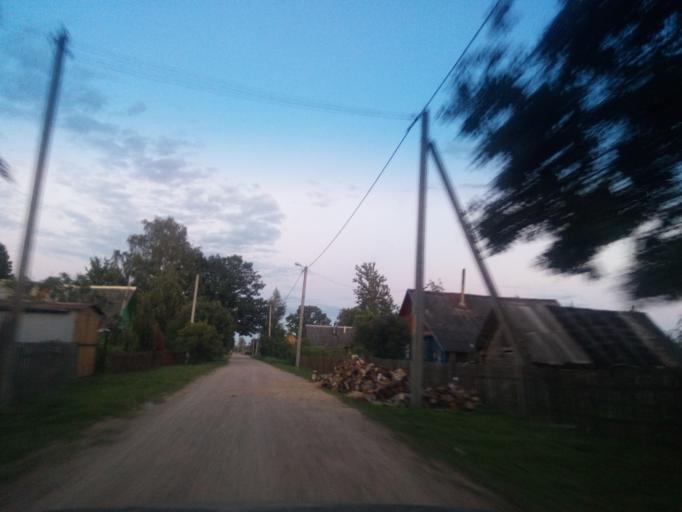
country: BY
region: Vitebsk
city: Dzisna
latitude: 55.6694
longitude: 28.3221
